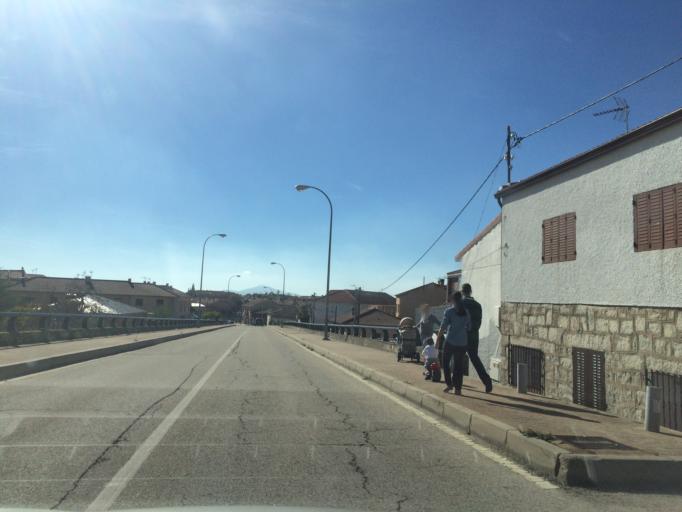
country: ES
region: Madrid
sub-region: Provincia de Madrid
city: La Cabrera
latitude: 40.8667
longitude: -3.6117
